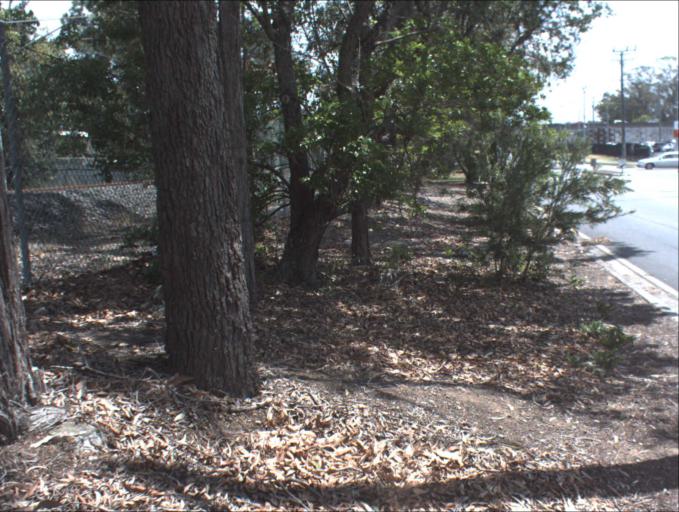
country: AU
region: Queensland
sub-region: Logan
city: Waterford West
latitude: -27.6714
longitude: 153.1415
